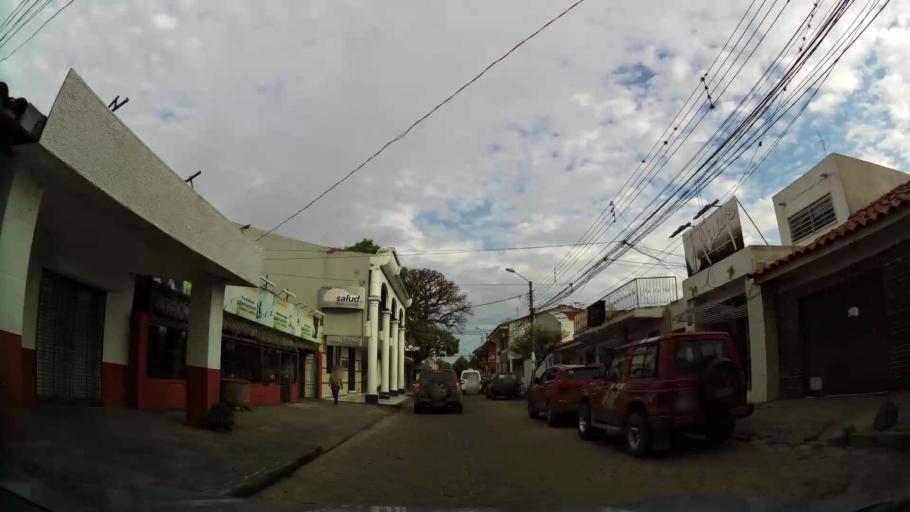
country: BO
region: Santa Cruz
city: Santa Cruz de la Sierra
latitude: -17.7862
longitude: -63.1731
